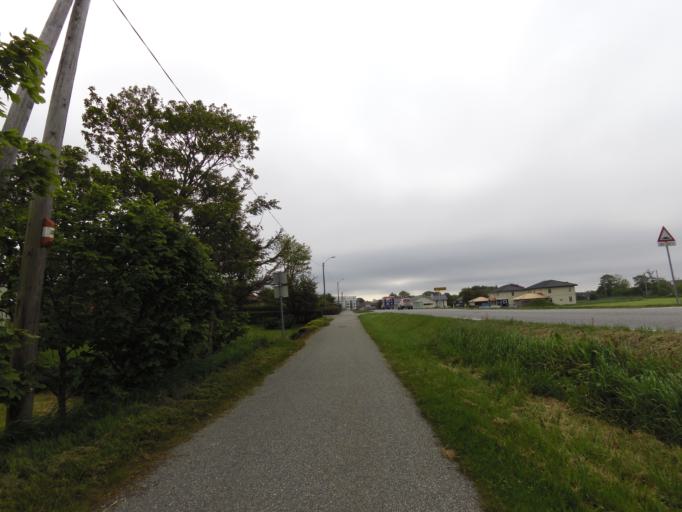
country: NO
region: Rogaland
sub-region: Ha
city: Vigrestad
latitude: 58.5729
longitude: 5.6830
